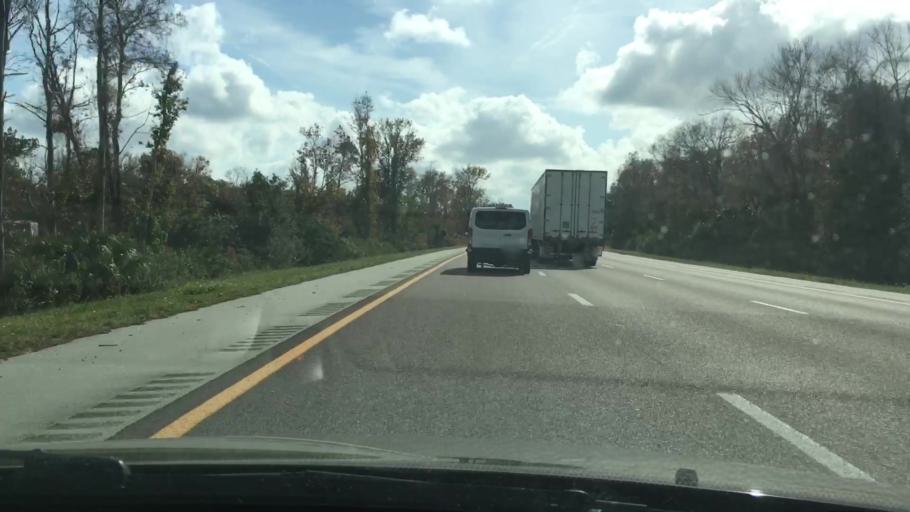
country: US
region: Florida
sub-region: Volusia County
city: Oak Hill
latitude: 28.8709
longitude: -80.9199
